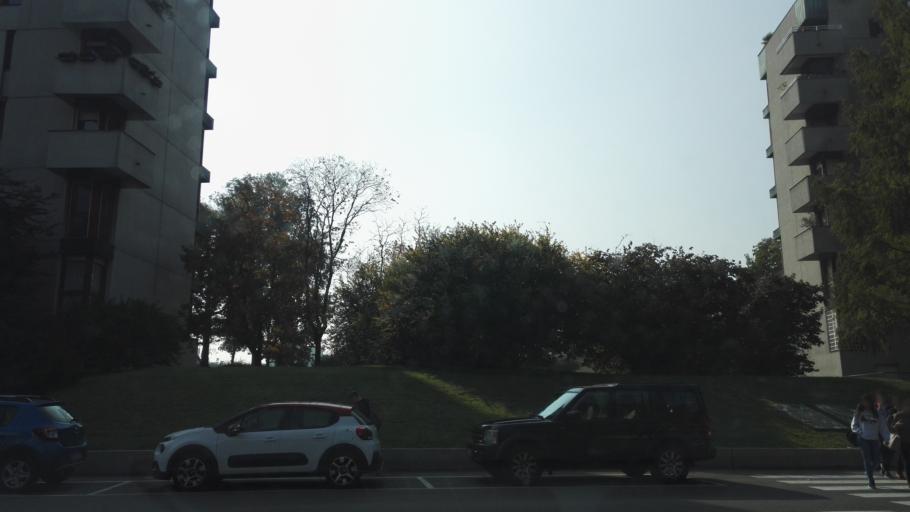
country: IT
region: Lombardy
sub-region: Citta metropolitana di Milano
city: San Bovio-San Felice
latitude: 45.4750
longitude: 9.3079
